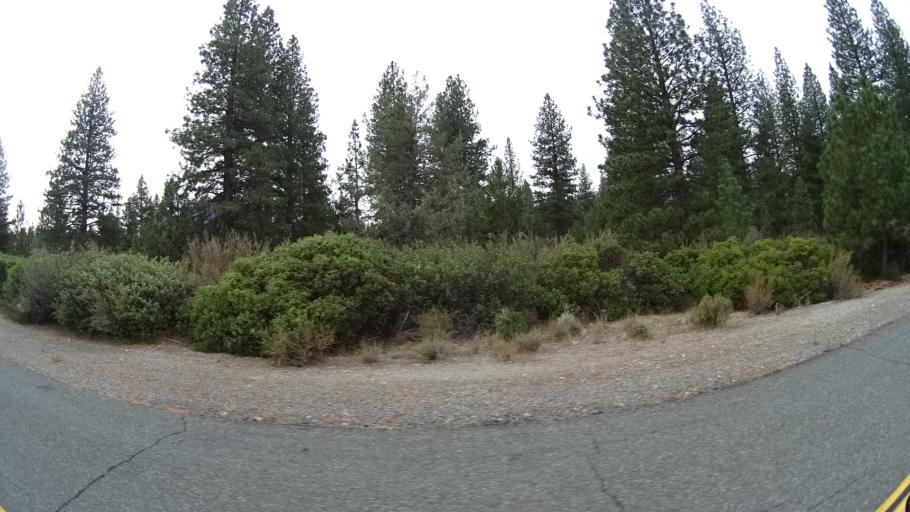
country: US
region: California
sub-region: Siskiyou County
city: Weed
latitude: 41.4128
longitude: -122.3659
